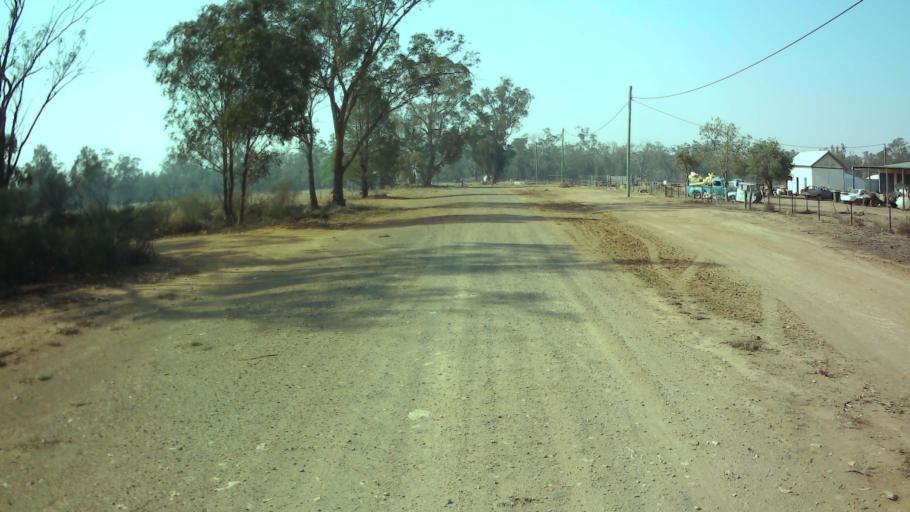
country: AU
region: New South Wales
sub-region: Weddin
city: Grenfell
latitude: -33.8460
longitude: 147.7386
